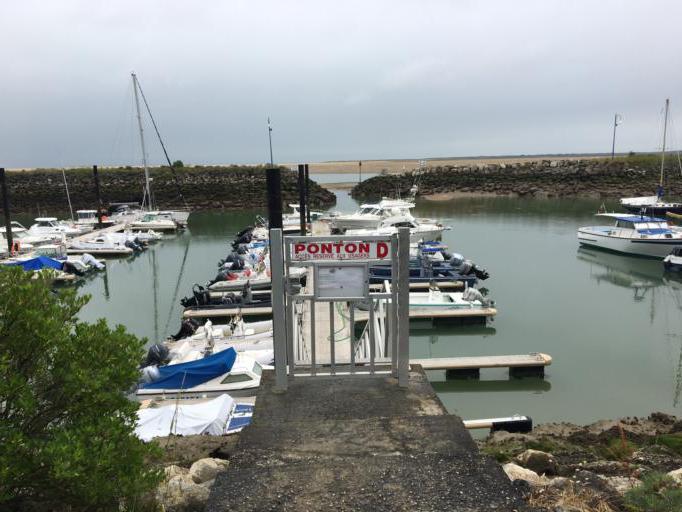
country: FR
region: Poitou-Charentes
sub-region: Departement de la Charente-Maritime
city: Les Mathes
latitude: 45.6849
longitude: -1.1831
